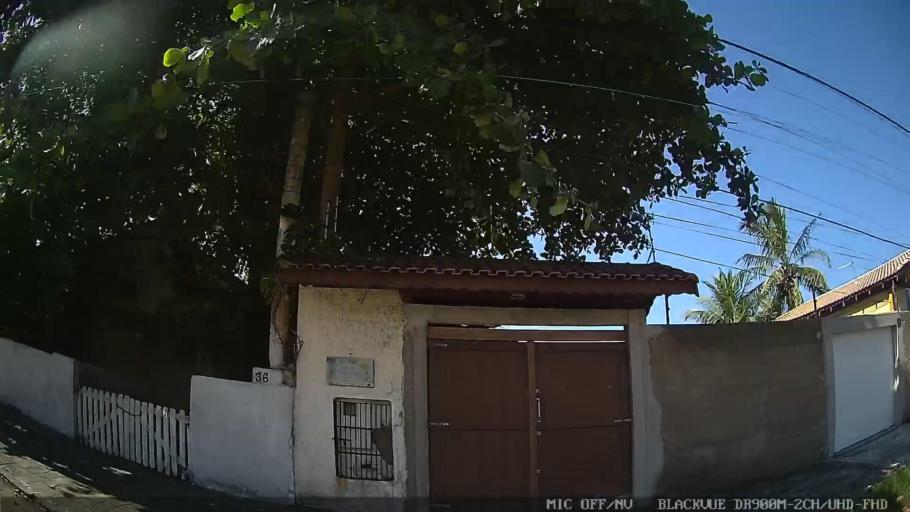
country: BR
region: Sao Paulo
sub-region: Peruibe
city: Peruibe
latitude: -24.3115
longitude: -46.9823
